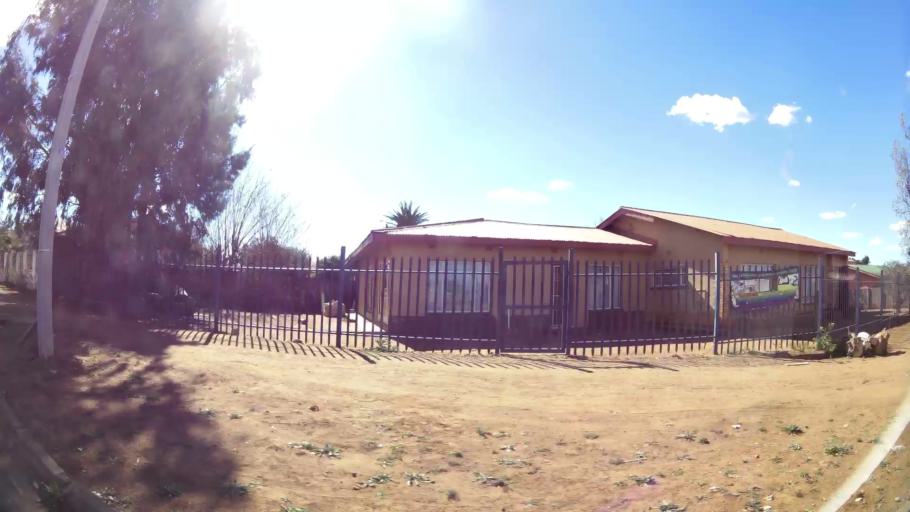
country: ZA
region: North-West
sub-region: Dr Kenneth Kaunda District Municipality
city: Klerksdorp
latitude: -26.8738
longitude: 26.5973
